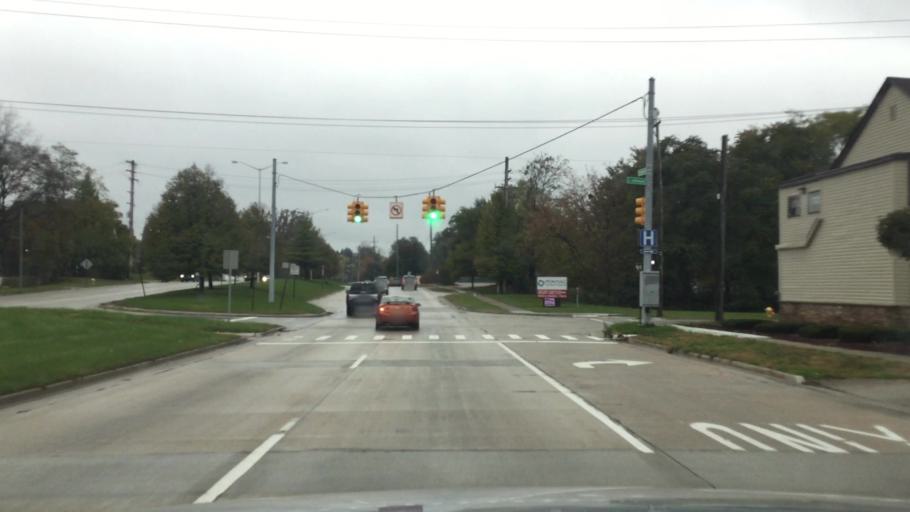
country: US
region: Michigan
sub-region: Oakland County
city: Pontiac
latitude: 42.6303
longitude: -83.3075
